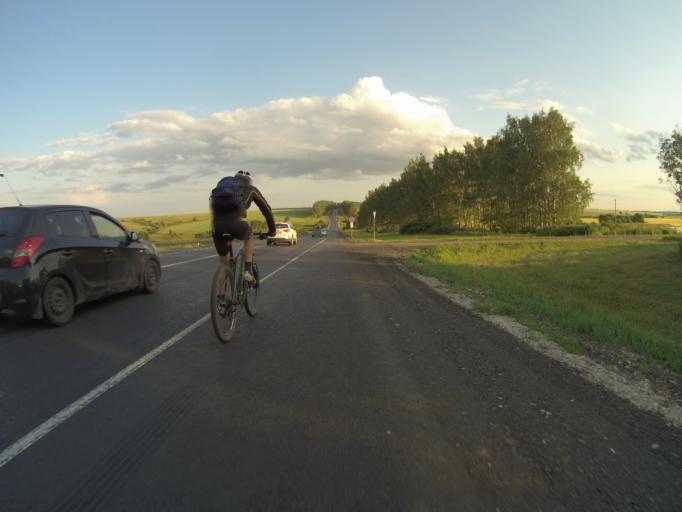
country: RU
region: Vladimir
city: Bogolyubovo
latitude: 56.2713
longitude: 40.4652
